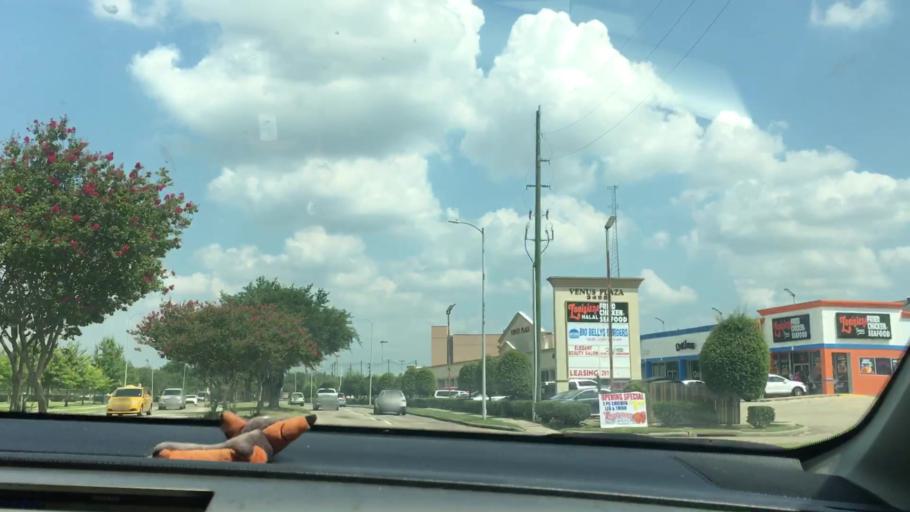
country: US
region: Texas
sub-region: Fort Bend County
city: Mission Bend
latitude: 29.7247
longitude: -95.6049
